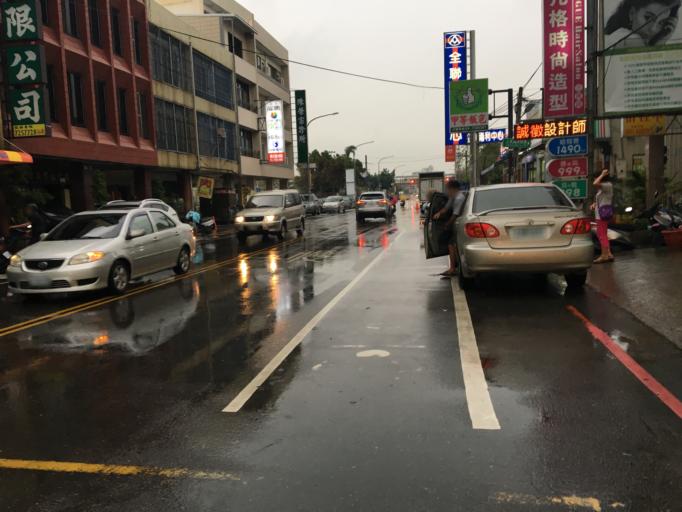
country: TW
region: Taiwan
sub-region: Changhua
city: Chang-hua
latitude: 24.0866
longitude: 120.5480
